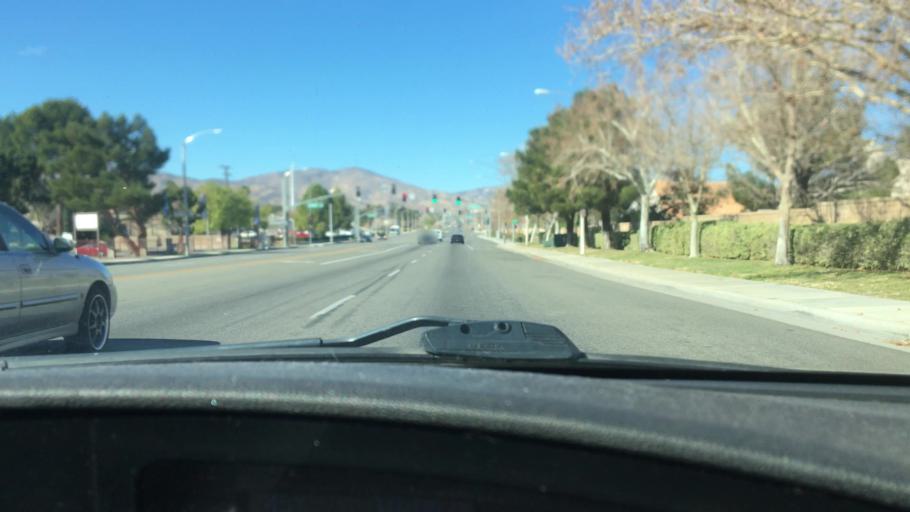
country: US
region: California
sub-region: Los Angeles County
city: Palmdale
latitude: 34.5581
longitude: -118.1038
